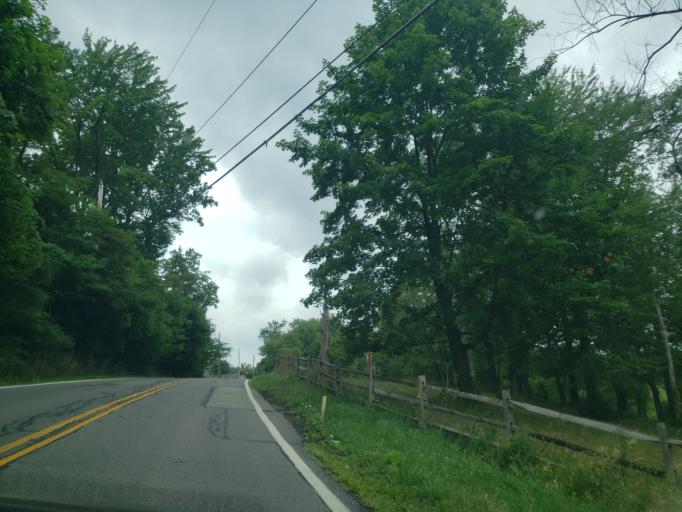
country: US
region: Pennsylvania
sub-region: Allegheny County
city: Coraopolis
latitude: 40.5332
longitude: -80.1407
